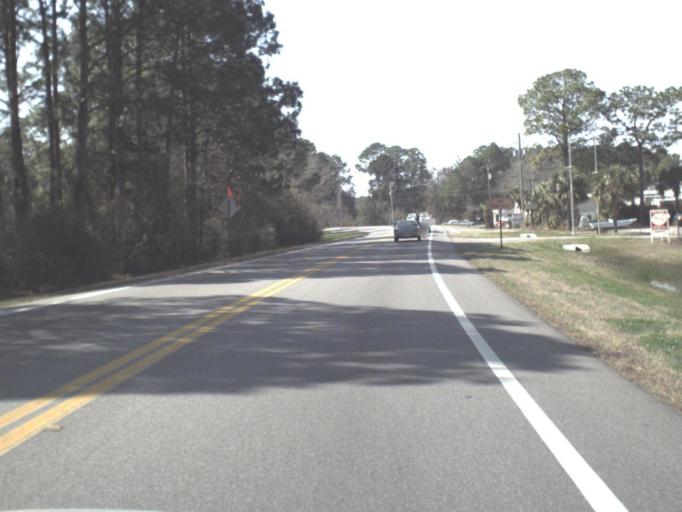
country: US
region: Florida
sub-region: Bay County
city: Pretty Bayou
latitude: 30.2034
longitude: -85.6763
